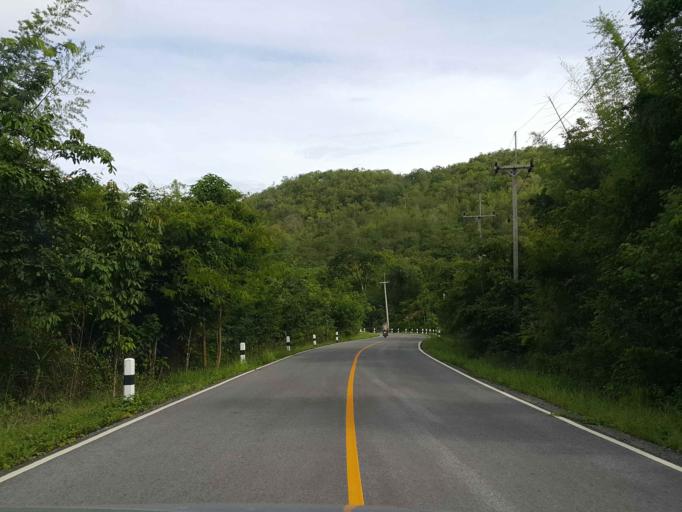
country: TH
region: Sukhothai
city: Thung Saliam
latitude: 17.2441
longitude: 99.4931
